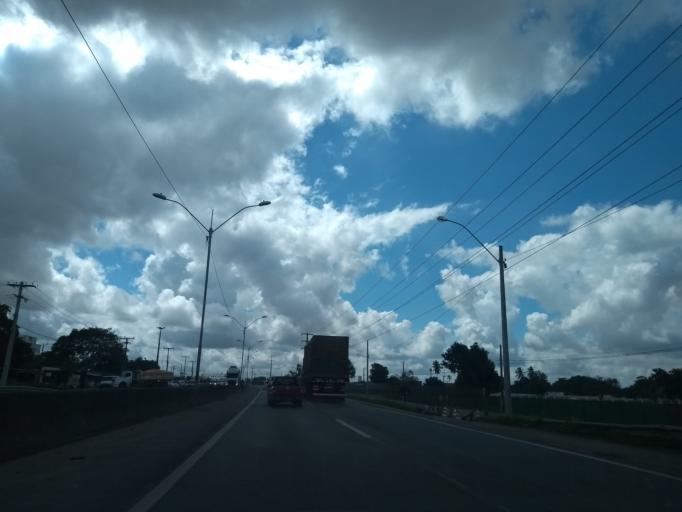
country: BR
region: Bahia
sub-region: Feira De Santana
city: Feira de Santana
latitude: -12.2784
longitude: -38.9406
